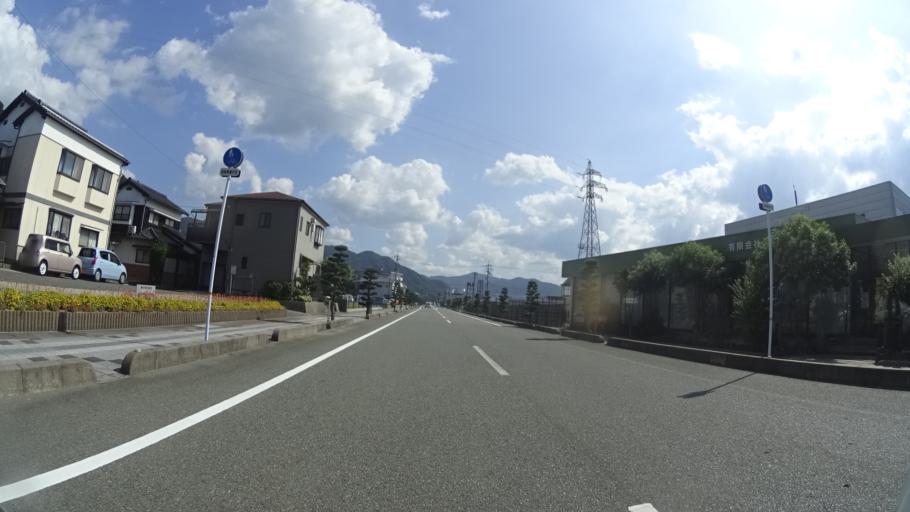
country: JP
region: Yamaguchi
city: Hagi
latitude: 34.4201
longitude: 131.4127
